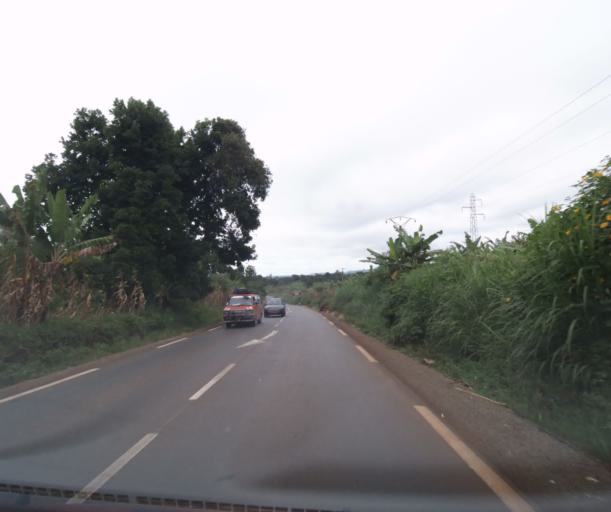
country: CM
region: West
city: Bansoa
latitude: 5.5351
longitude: 10.3279
